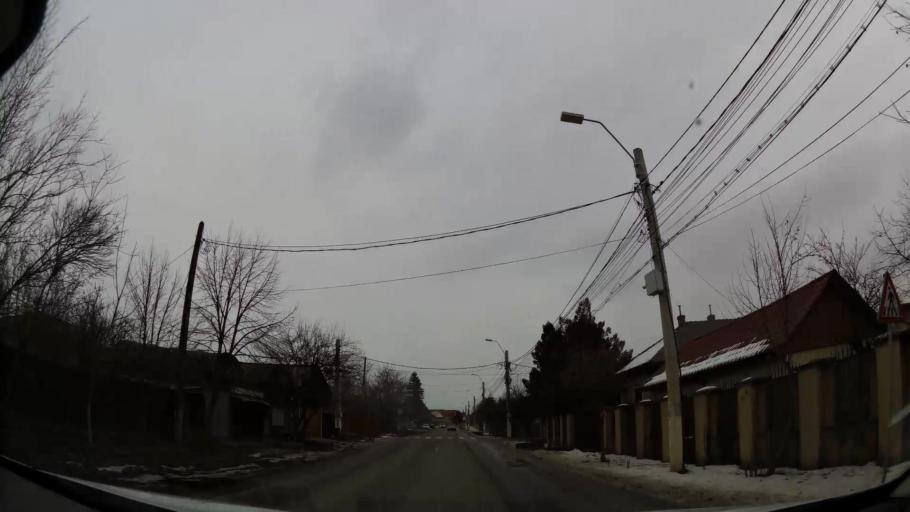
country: RO
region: Ilfov
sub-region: Comuna Tunari
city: Tunari
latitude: 44.5487
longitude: 26.1274
